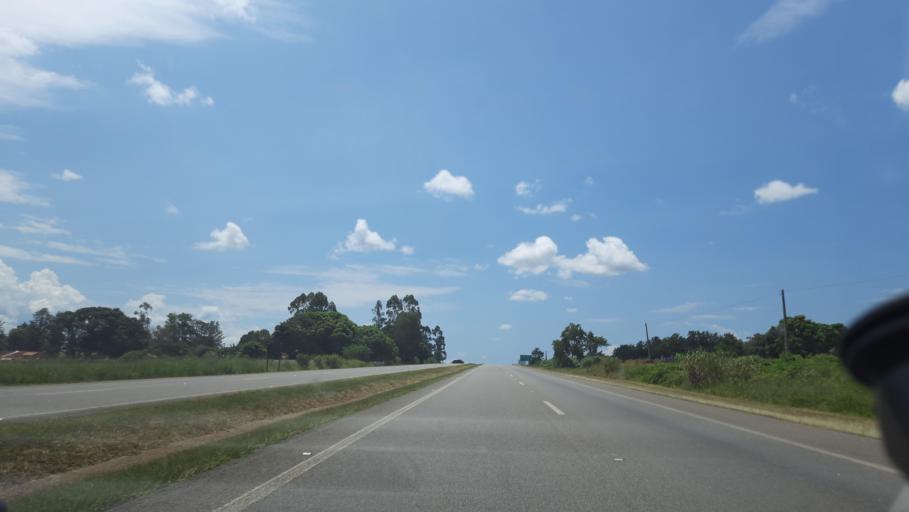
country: BR
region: Sao Paulo
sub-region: Mococa
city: Mococa
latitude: -21.5800
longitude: -47.0376
